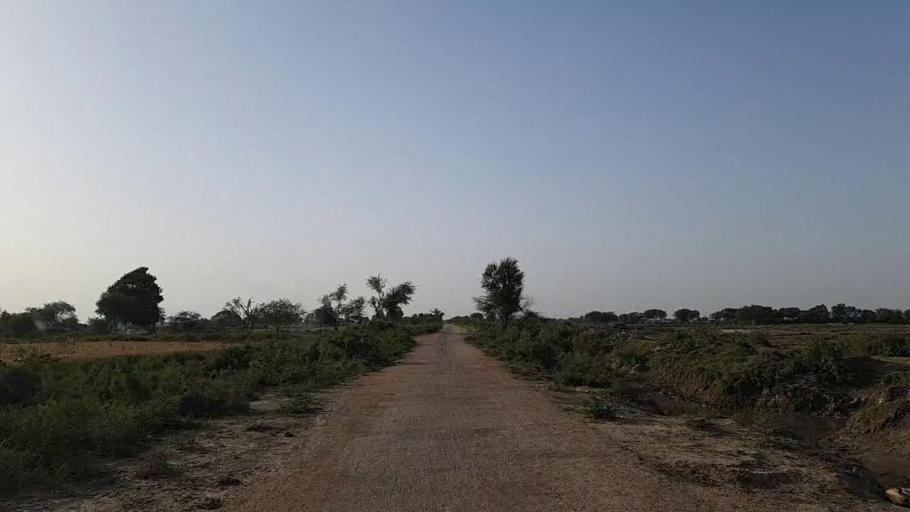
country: PK
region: Sindh
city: Jati
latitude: 24.3252
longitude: 68.1642
